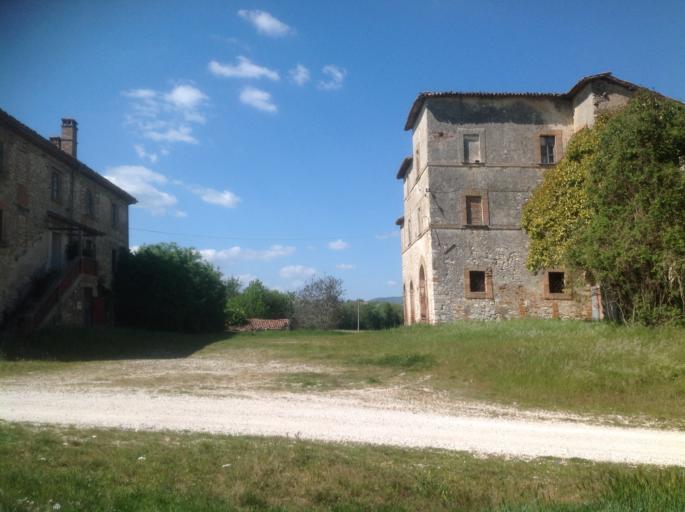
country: IT
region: Latium
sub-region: Provincia di Rieti
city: Limiti di Greccio
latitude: 42.4682
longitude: 12.7950
